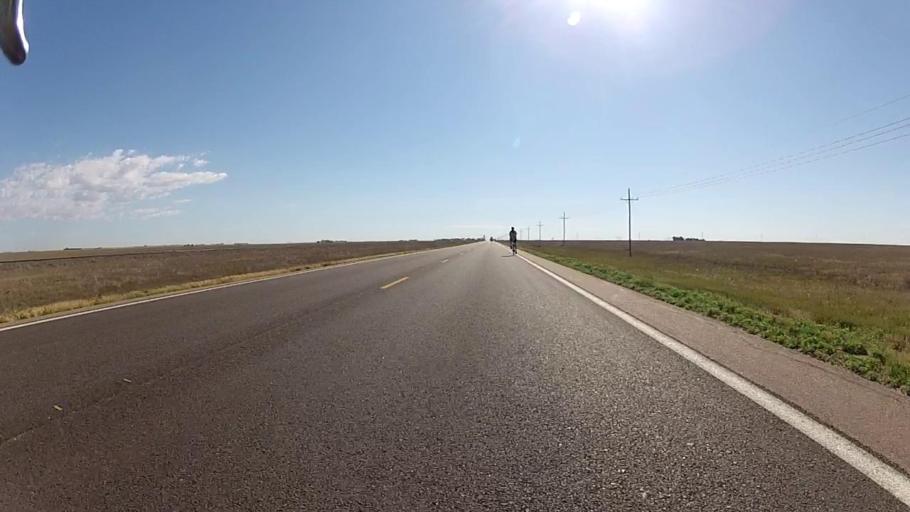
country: US
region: Kansas
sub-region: Gray County
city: Cimarron
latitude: 37.5821
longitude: -100.5038
